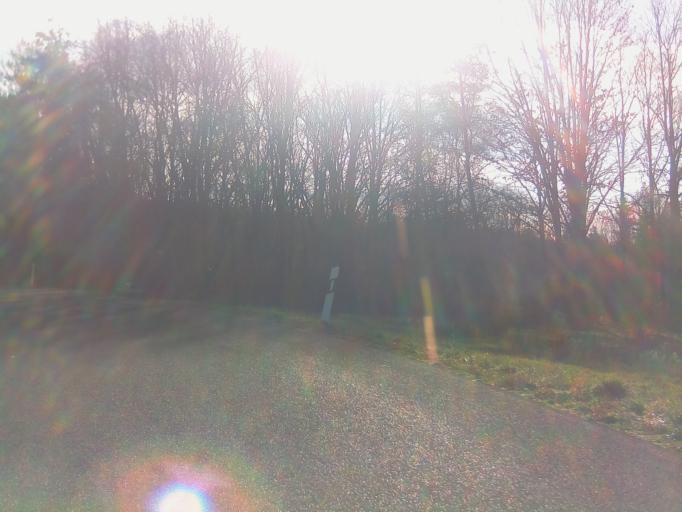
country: DE
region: Bavaria
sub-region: Regierungsbezirk Unterfranken
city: Neunkirchen
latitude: 49.7986
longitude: 9.4097
